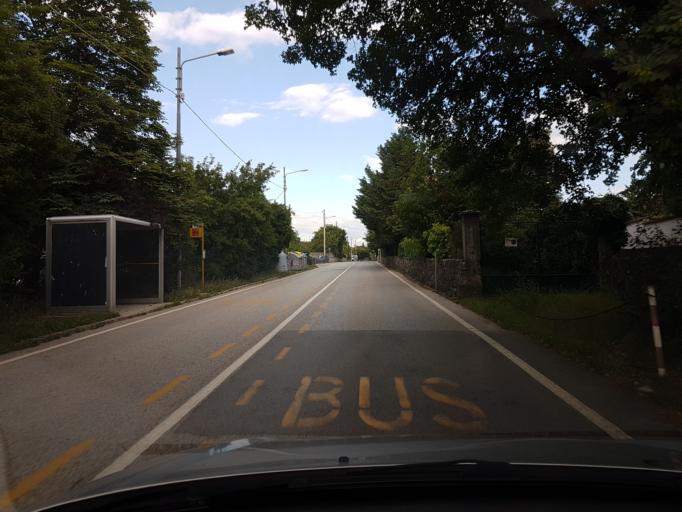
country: IT
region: Friuli Venezia Giulia
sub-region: Provincia di Trieste
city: Villa Opicina
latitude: 45.6851
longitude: 13.7960
